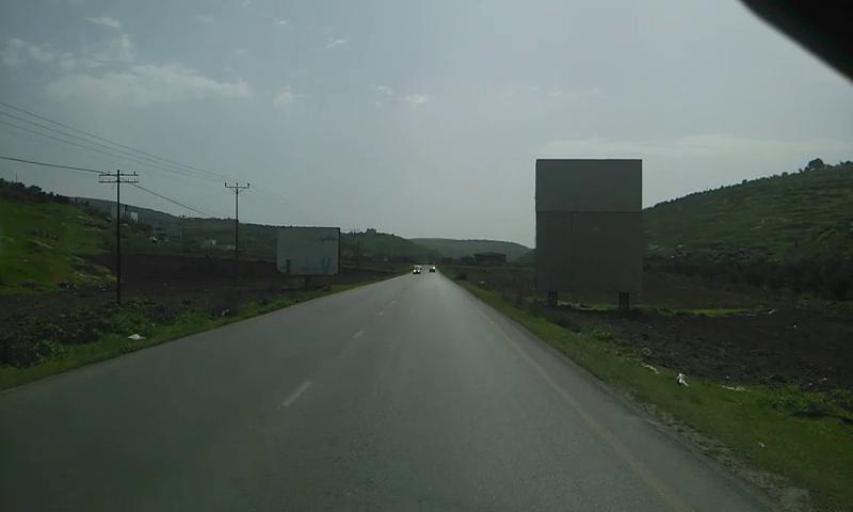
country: PS
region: West Bank
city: Mirkah
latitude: 32.3964
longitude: 35.2219
